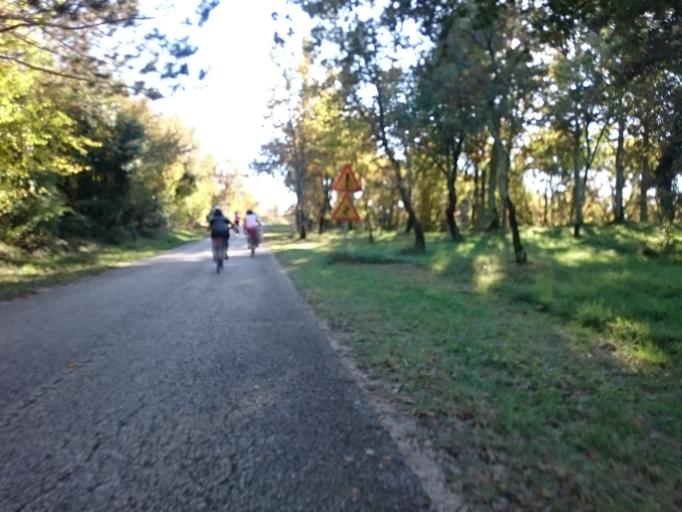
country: HR
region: Istarska
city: Buje
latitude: 45.4100
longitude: 13.7225
